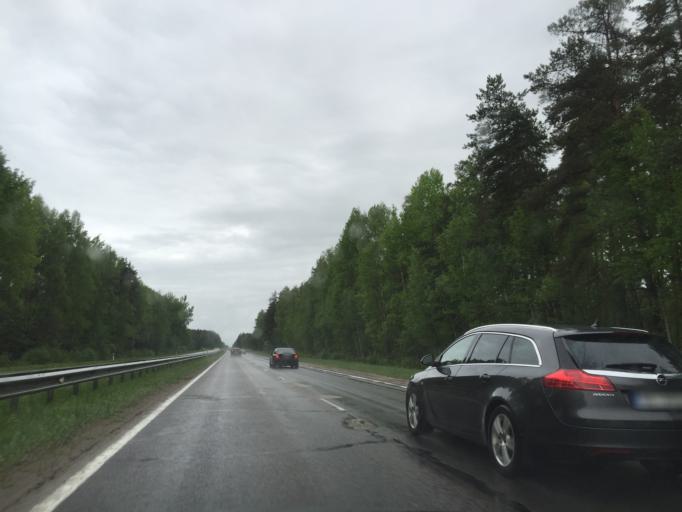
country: LV
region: Ikskile
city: Ikskile
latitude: 56.8255
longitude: 24.5275
